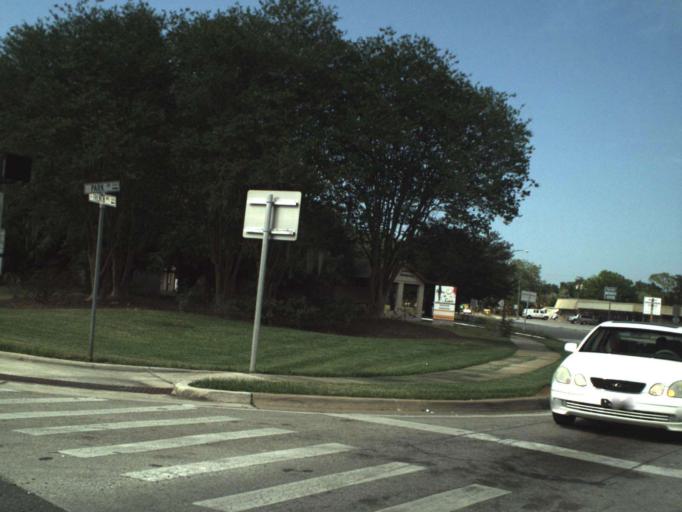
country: US
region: Florida
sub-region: Seminole County
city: Sanford
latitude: 28.7820
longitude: -81.2729
